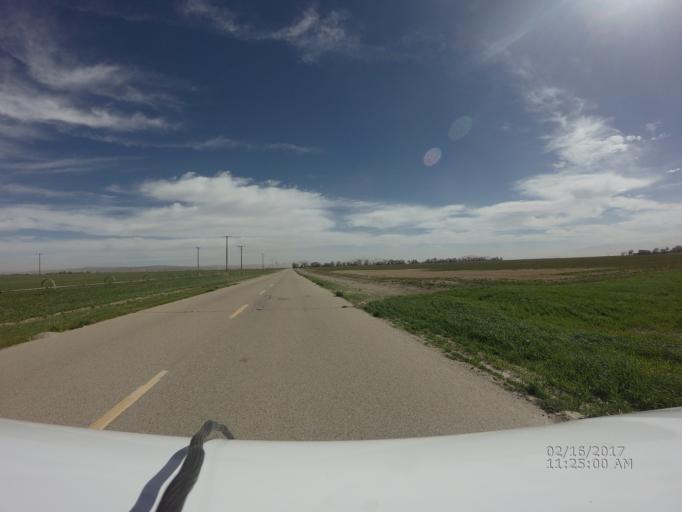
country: US
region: California
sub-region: Los Angeles County
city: Lake Los Angeles
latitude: 34.7047
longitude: -117.9309
